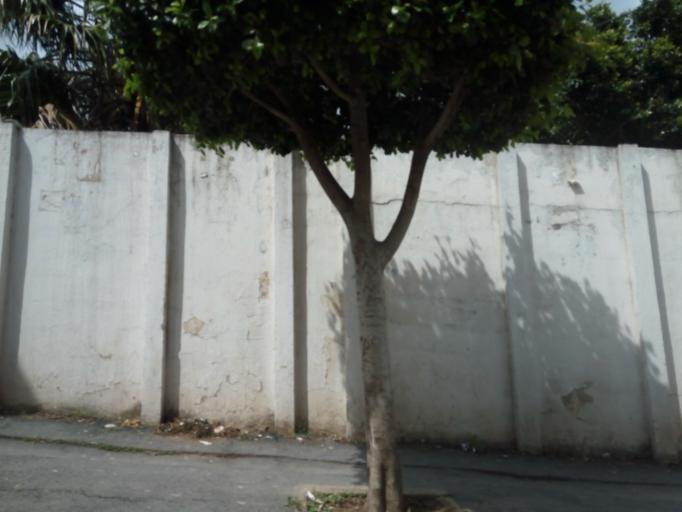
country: DZ
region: Tipaza
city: Douera
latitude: 36.6992
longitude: 2.9760
